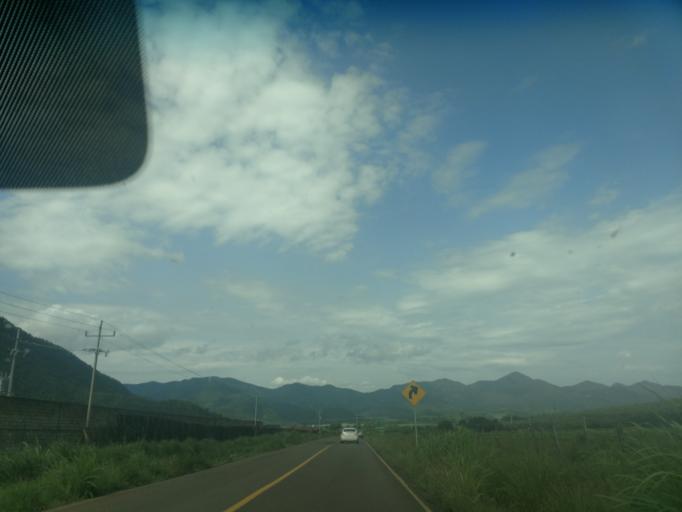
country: MX
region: Jalisco
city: Talpa de Allende
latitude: 20.4216
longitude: -104.7228
